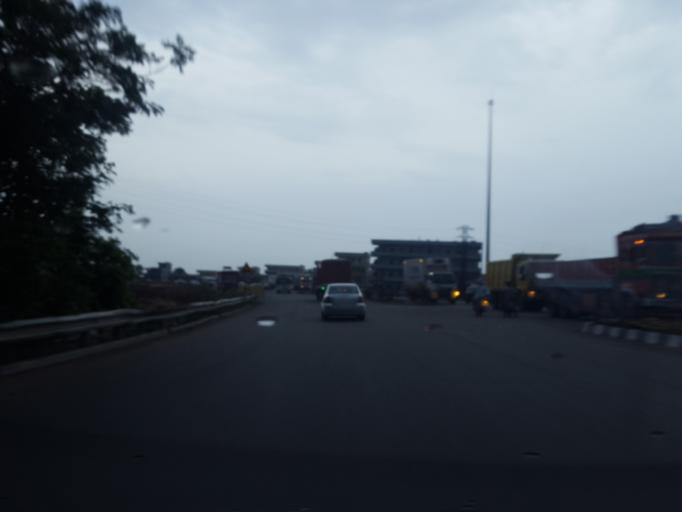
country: IN
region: Telangana
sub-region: Mahbubnagar
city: Farrukhnagar
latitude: 17.1511
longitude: 78.2907
